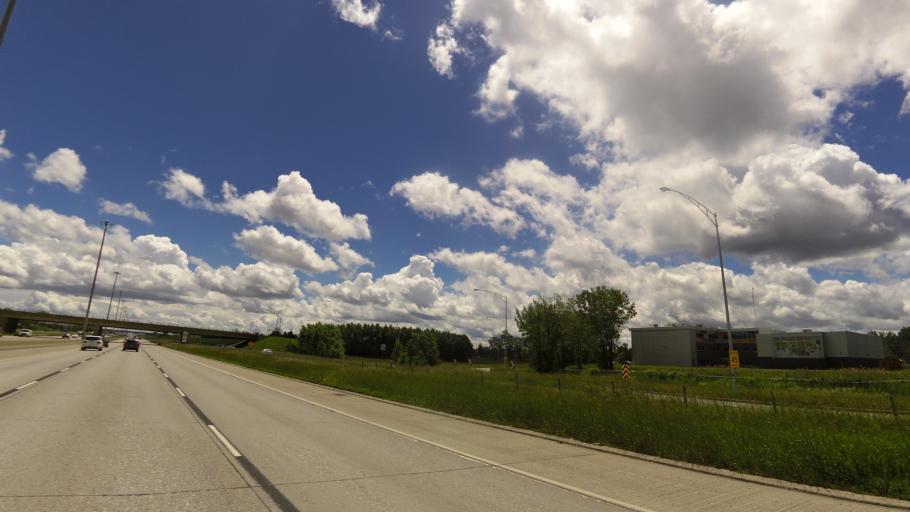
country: CA
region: Quebec
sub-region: Laurentides
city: Boisbriand
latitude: 45.5751
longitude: -73.8316
